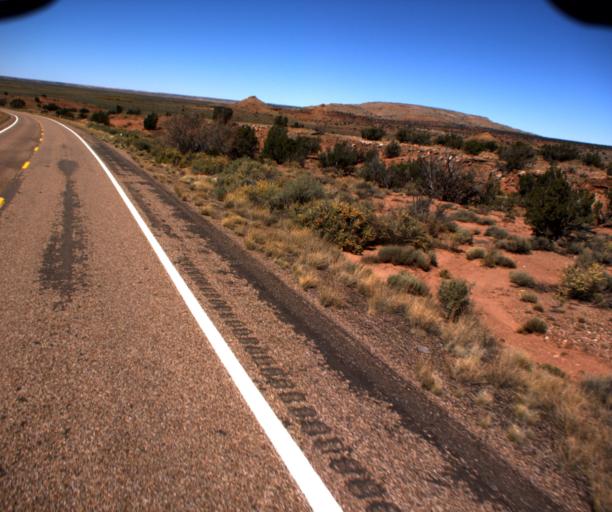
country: US
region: Arizona
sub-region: Apache County
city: Saint Johns
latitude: 34.5845
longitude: -109.5402
